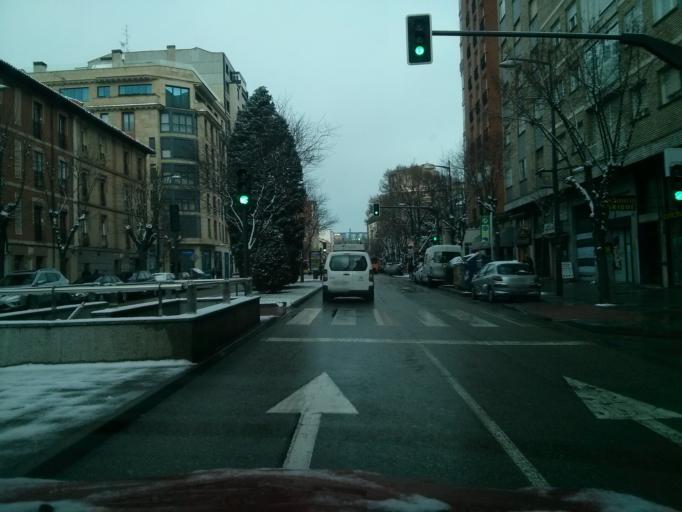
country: ES
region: Castille and Leon
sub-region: Provincia de Burgos
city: Burgos
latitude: 42.3469
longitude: -3.6973
